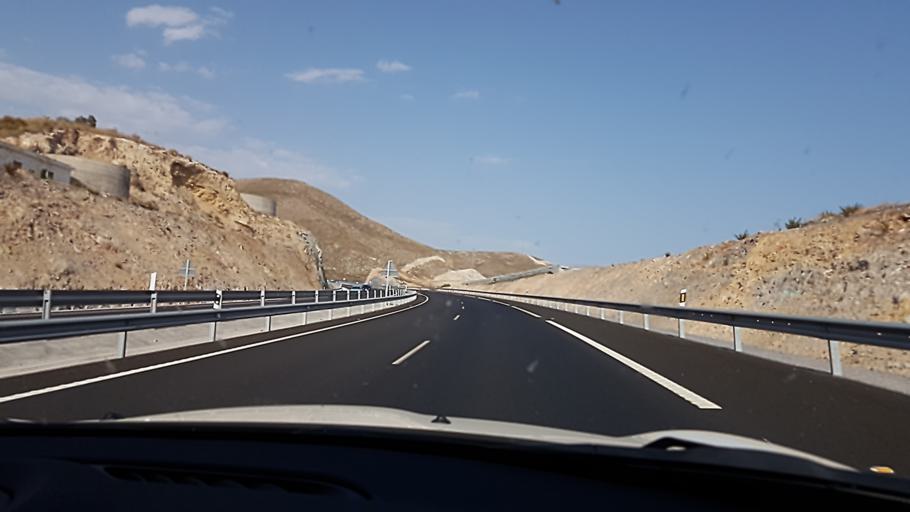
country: ES
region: Andalusia
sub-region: Provincia de Granada
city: Gualchos
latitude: 36.7116
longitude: -3.4020
